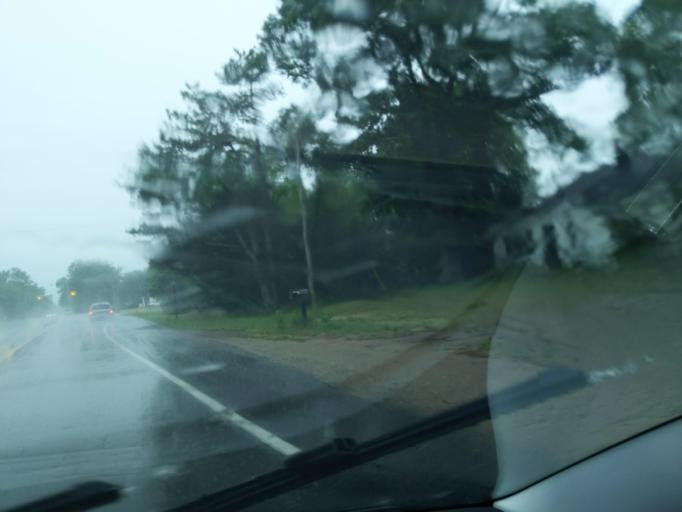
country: US
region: Michigan
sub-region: Muskegon County
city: Fruitport
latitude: 43.1498
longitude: -86.1640
